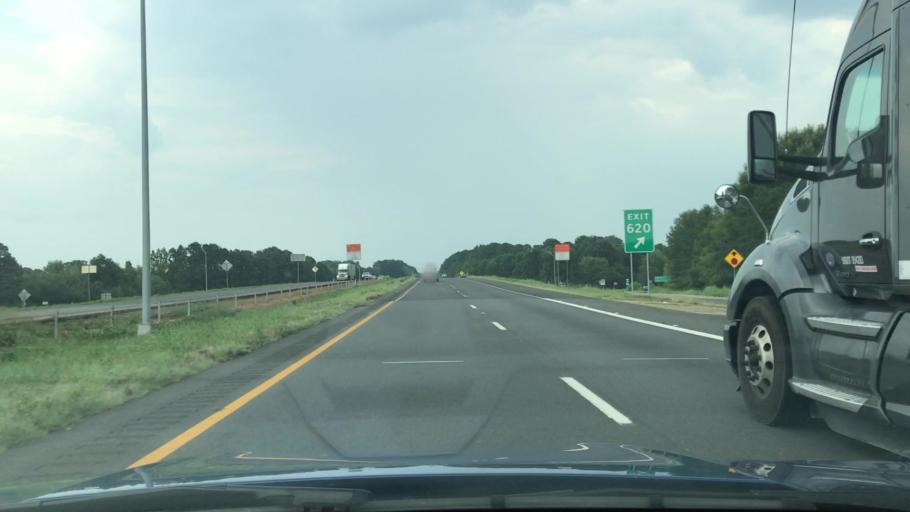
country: US
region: Texas
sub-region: Harrison County
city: Marshall
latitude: 32.4935
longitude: -94.2995
